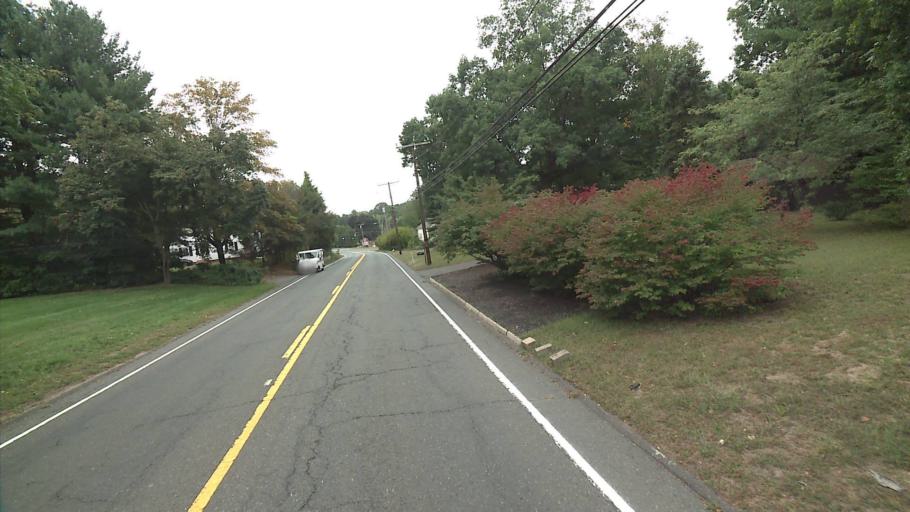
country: US
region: Connecticut
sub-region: Hartford County
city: Windsor Locks
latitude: 41.9104
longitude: -72.6781
